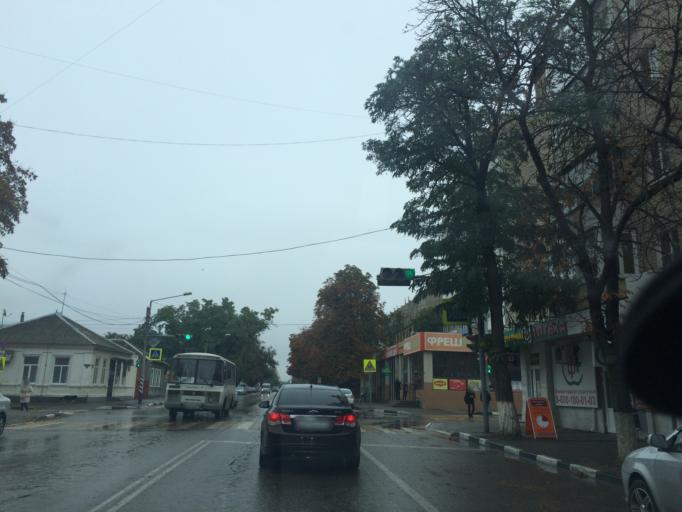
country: RU
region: Rostov
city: Azov
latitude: 47.1109
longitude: 39.4252
